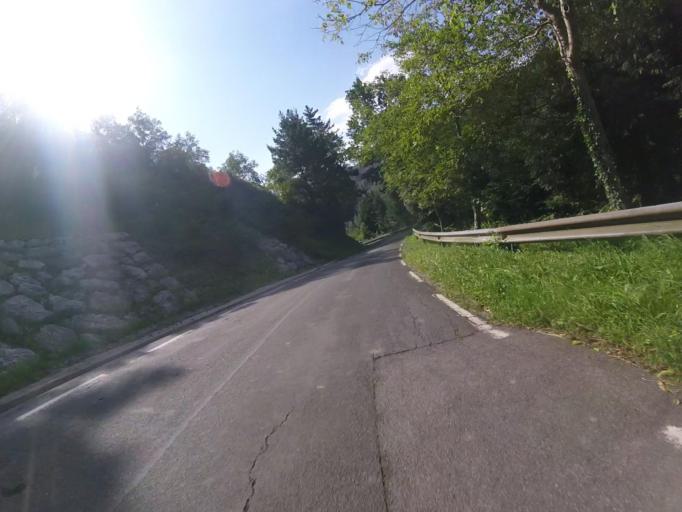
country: ES
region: Basque Country
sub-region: Provincia de Guipuzcoa
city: Alquiza
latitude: 43.1700
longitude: -2.1042
